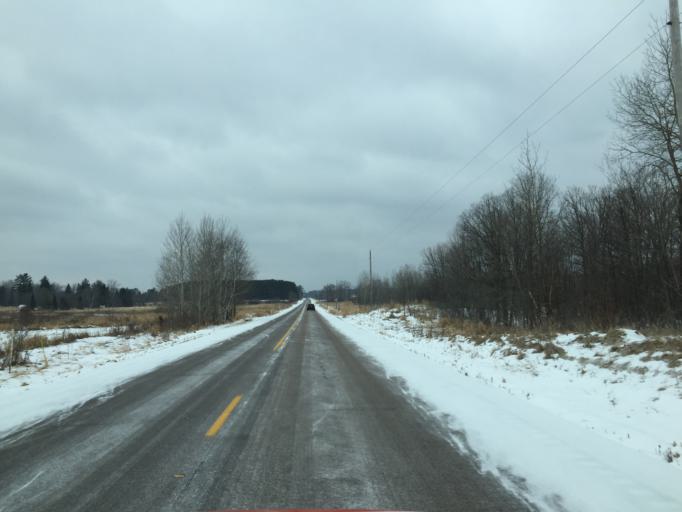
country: US
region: Minnesota
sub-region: Mille Lacs County
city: Vineland
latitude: 46.0774
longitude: -93.7346
